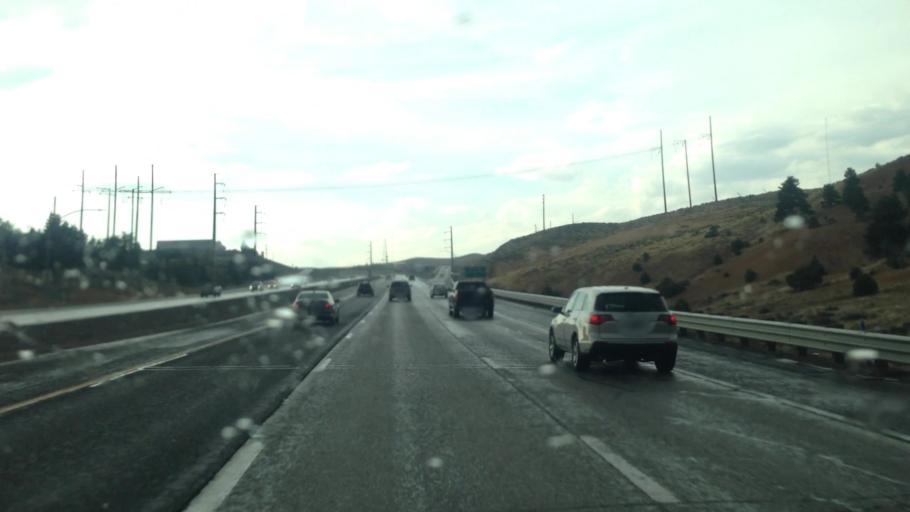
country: US
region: Nevada
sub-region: Washoe County
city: Reno
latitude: 39.5677
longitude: -119.8034
